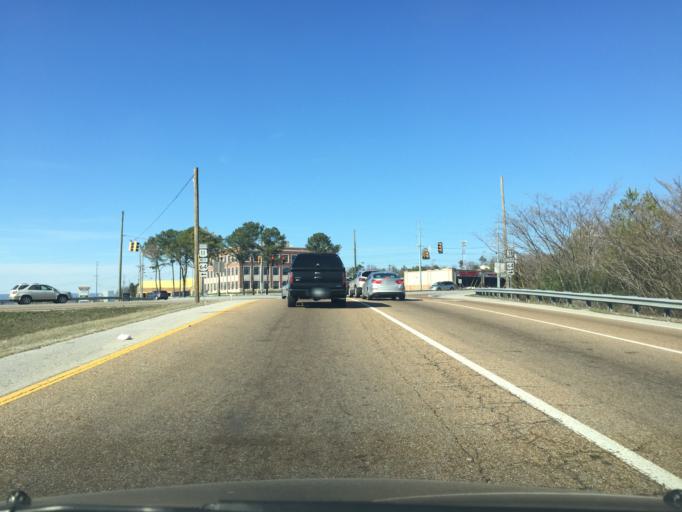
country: US
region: Tennessee
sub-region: Hamilton County
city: East Brainerd
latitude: 35.0322
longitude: -85.1816
